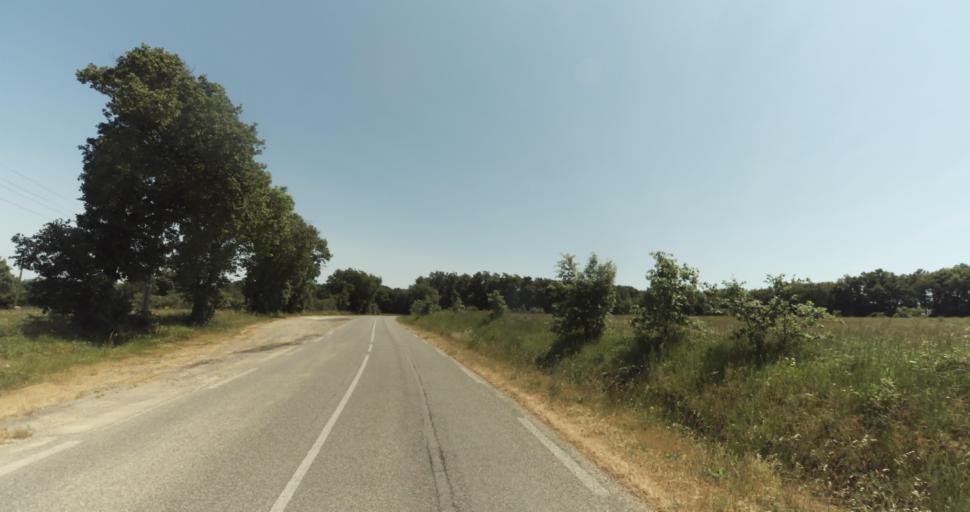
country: FR
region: Midi-Pyrenees
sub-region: Departement de la Haute-Garonne
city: Levignac
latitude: 43.6259
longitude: 1.1850
